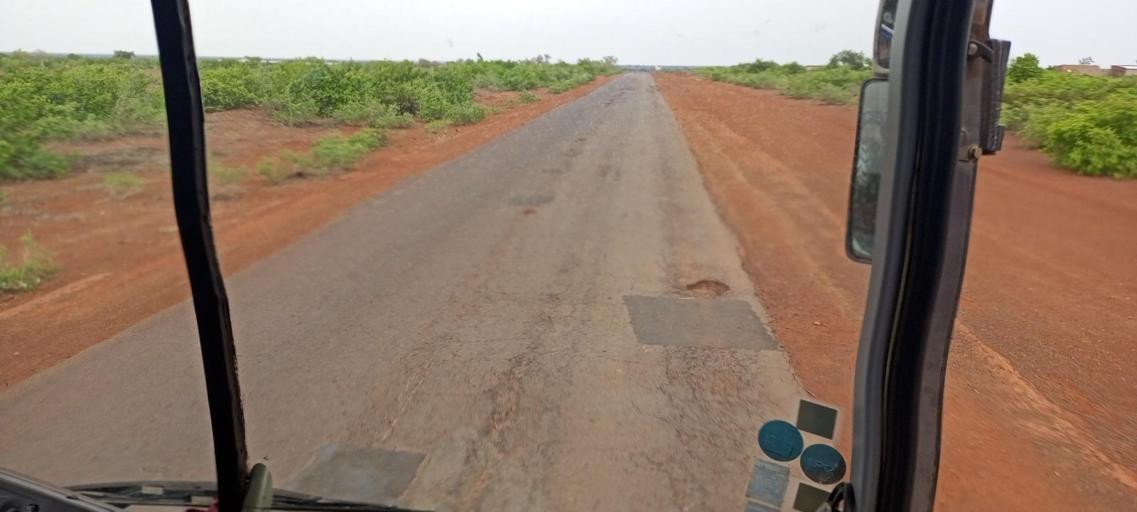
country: ML
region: Segou
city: Bla
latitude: 12.7004
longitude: -5.7240
